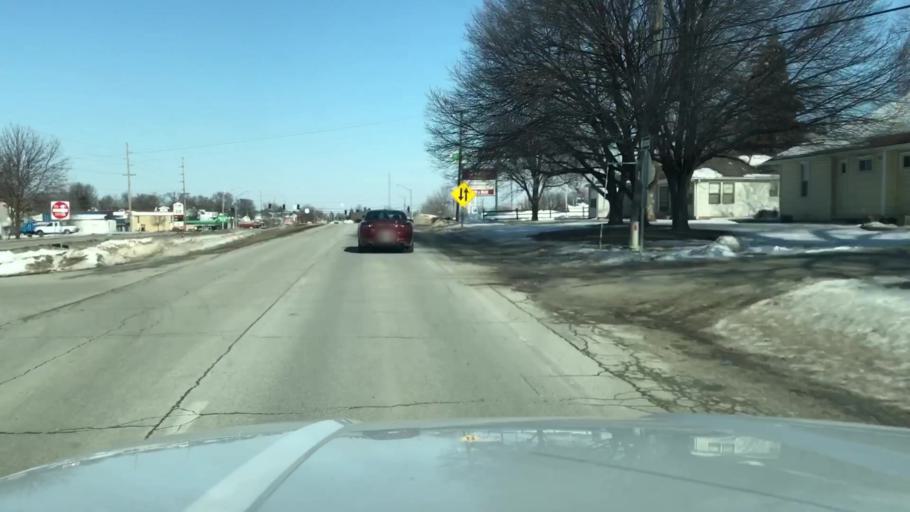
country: US
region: Missouri
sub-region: Andrew County
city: Savannah
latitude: 39.9373
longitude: -94.8218
